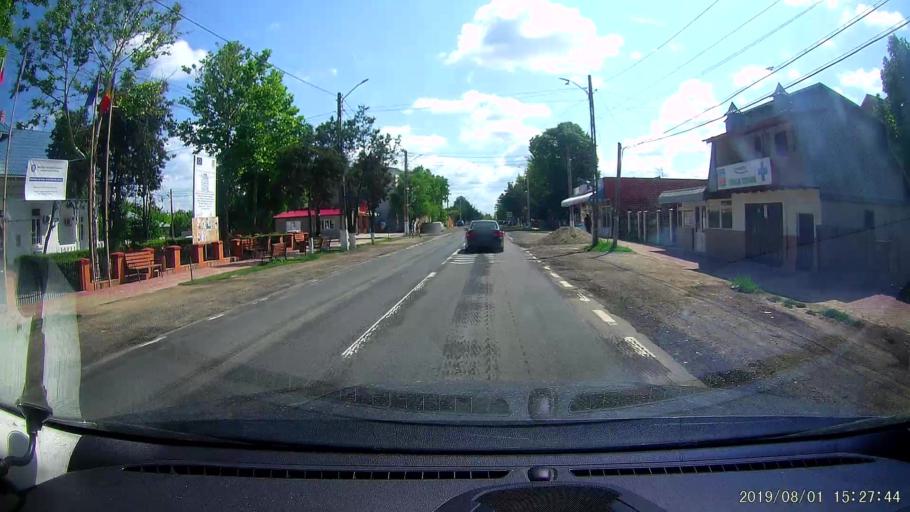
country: RO
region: Braila
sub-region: Comuna Viziru
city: Viziru
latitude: 44.9991
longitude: 27.7138
